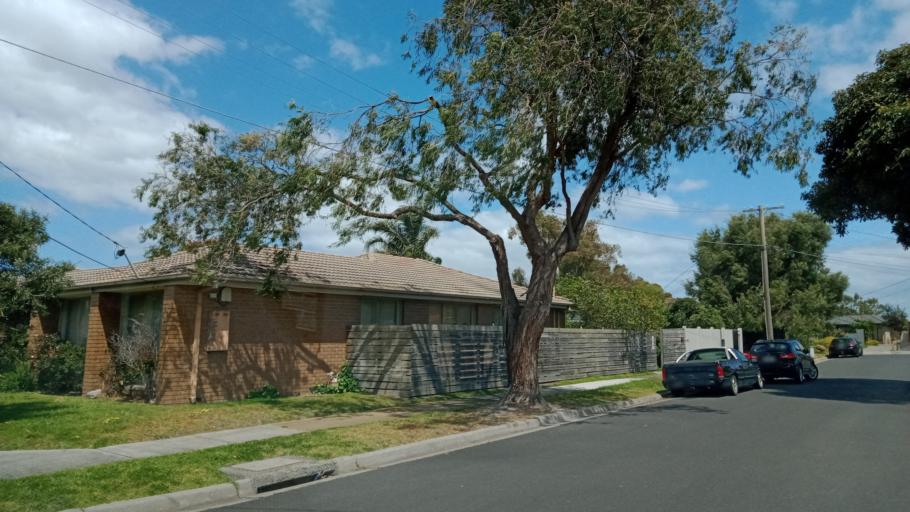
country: AU
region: Victoria
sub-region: Kingston
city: Chelsea Heights
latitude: -38.0499
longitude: 145.1364
